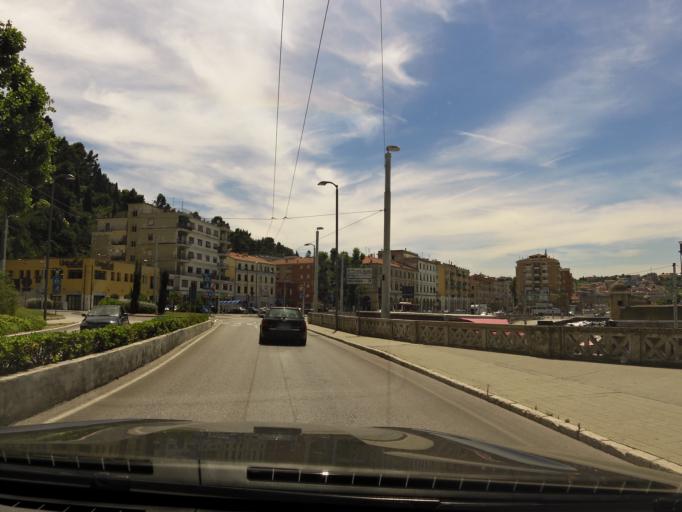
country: IT
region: The Marches
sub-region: Provincia di Ancona
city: Le Grazie di Ancona
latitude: 43.6149
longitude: 13.5051
